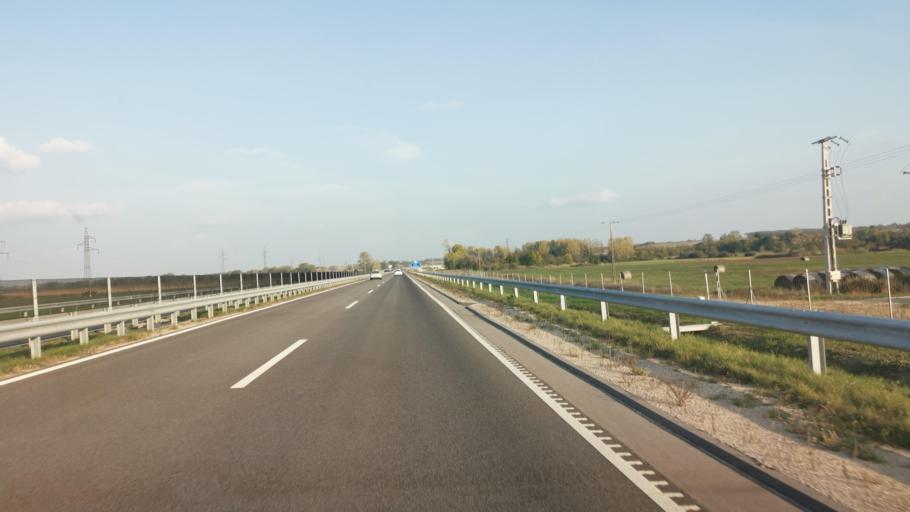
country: HU
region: Gyor-Moson-Sopron
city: Fertoszentmiklos
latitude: 47.5694
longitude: 16.8388
